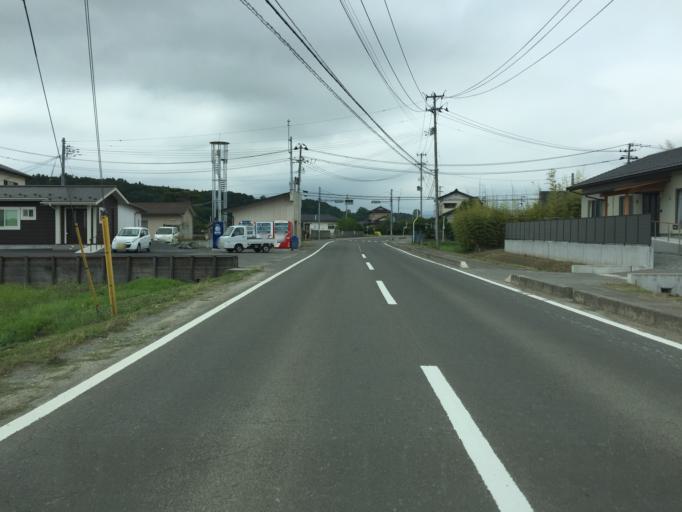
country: JP
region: Fukushima
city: Namie
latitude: 37.6895
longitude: 140.9833
